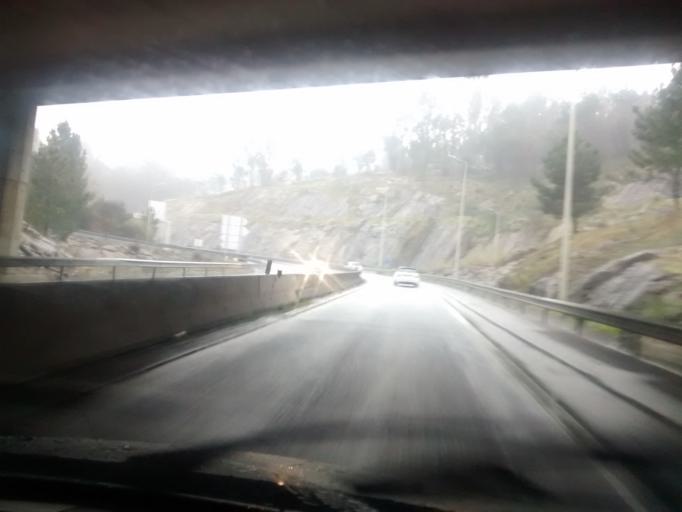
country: PT
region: Braga
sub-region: Braga
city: Braga
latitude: 41.5161
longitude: -8.4447
